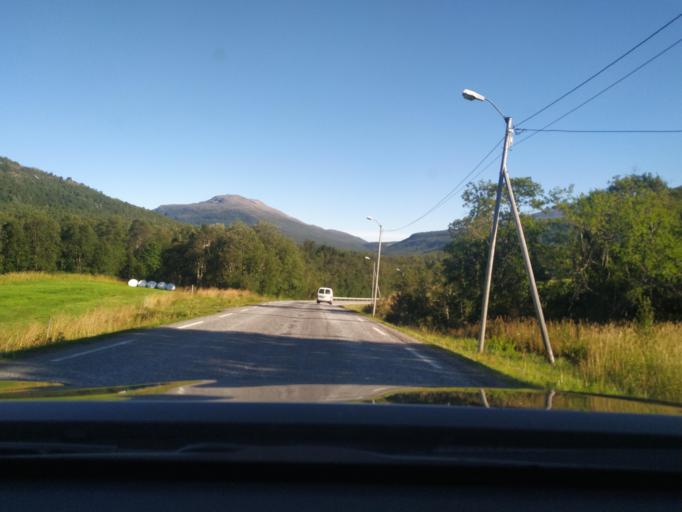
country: NO
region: Troms
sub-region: Salangen
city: Sjovegan
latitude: 68.9358
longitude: 17.7277
